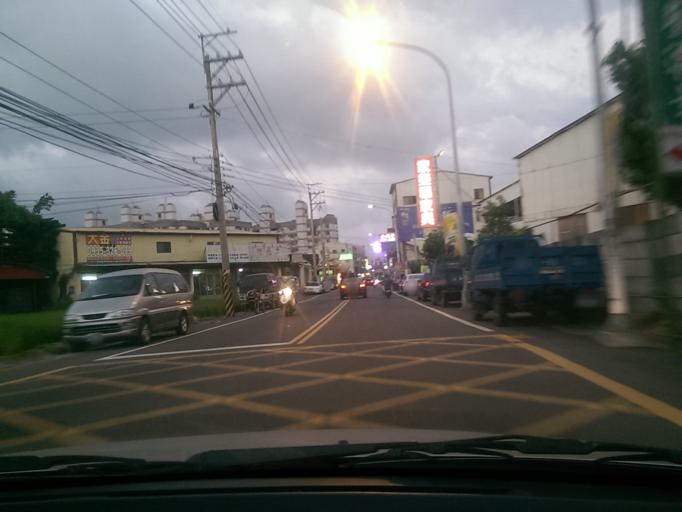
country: TW
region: Taiwan
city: Fengyuan
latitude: 24.2204
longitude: 120.6436
